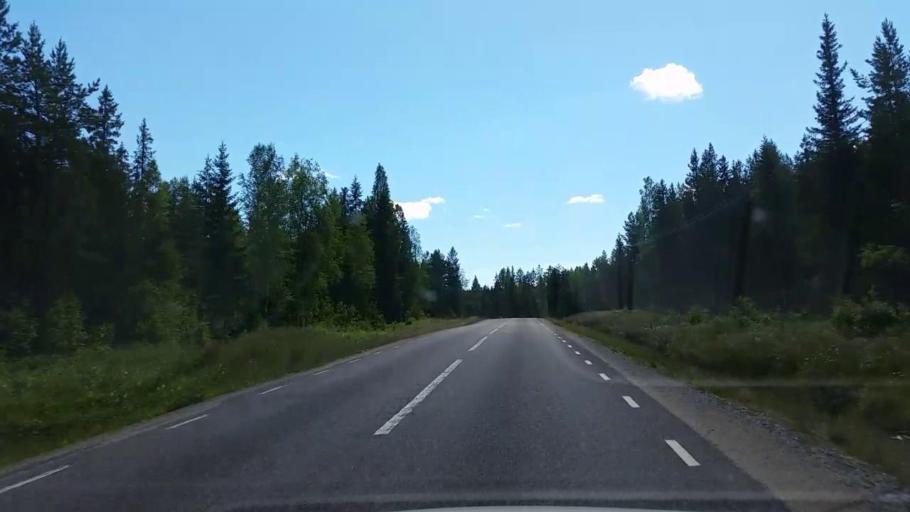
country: SE
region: Gaevleborg
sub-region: Ovanakers Kommun
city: Edsbyn
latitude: 61.5322
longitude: 15.6790
